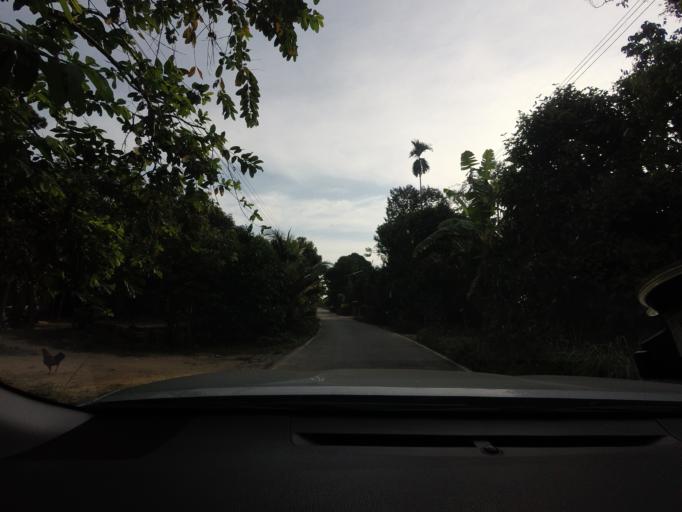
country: TH
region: Narathiwat
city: Ra-ngae
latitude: 6.2984
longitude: 101.7661
